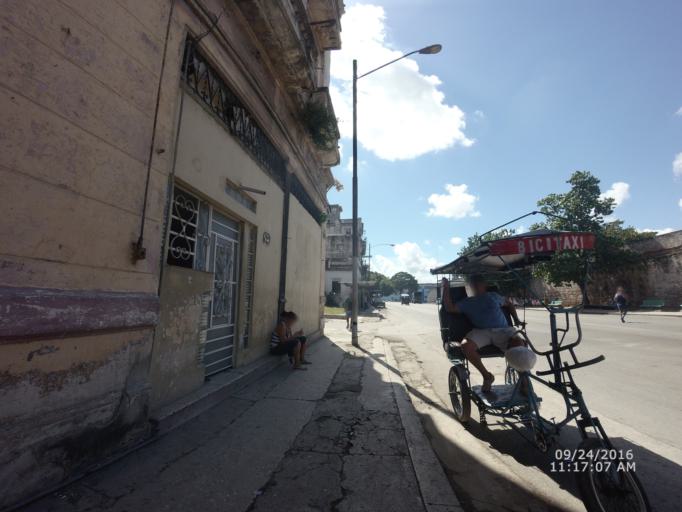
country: CU
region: La Habana
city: La Habana Vieja
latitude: 23.1297
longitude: -82.3535
